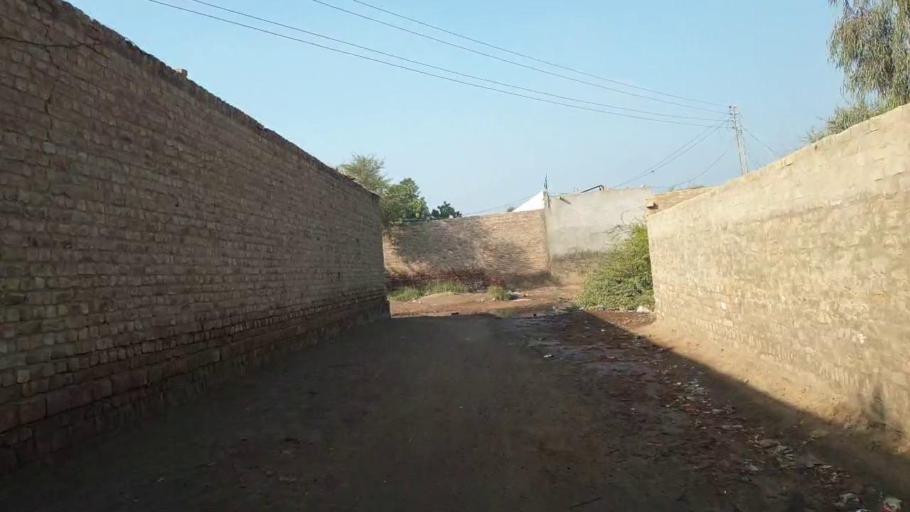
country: PK
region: Sindh
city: Shahdadpur
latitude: 25.9719
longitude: 68.6080
